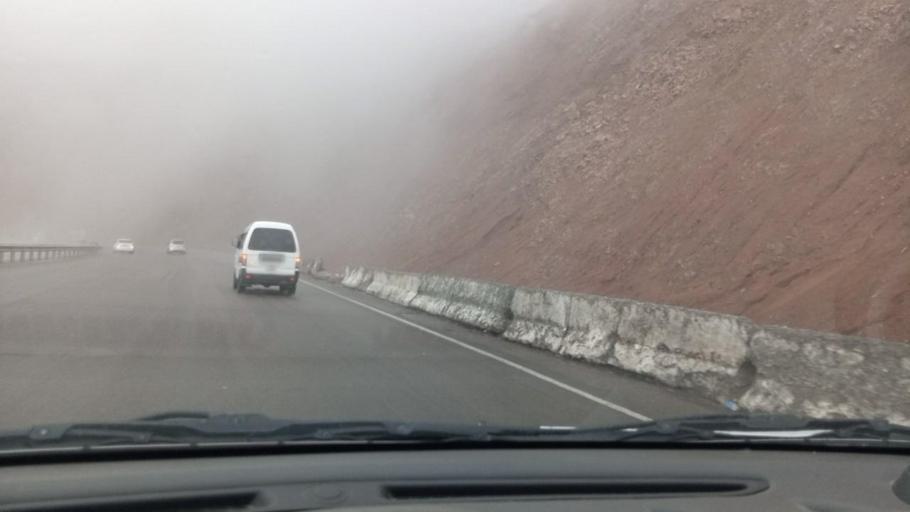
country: UZ
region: Toshkent
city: Angren
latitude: 41.1115
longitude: 70.5049
